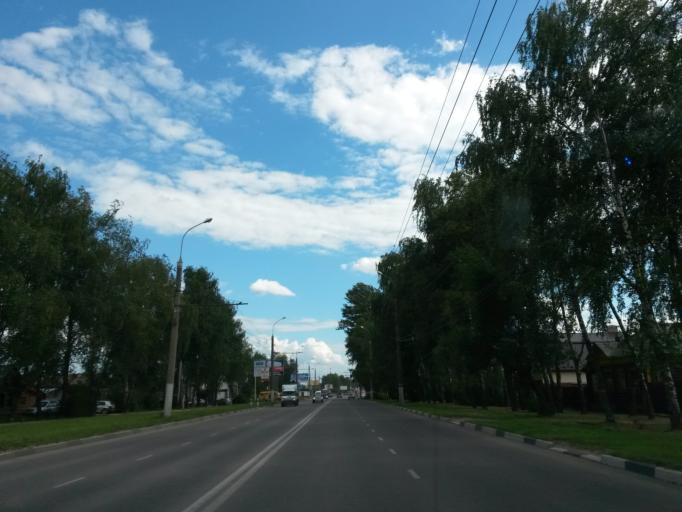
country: RU
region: Ivanovo
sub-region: Gorod Ivanovo
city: Ivanovo
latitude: 56.9808
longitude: 40.9990
